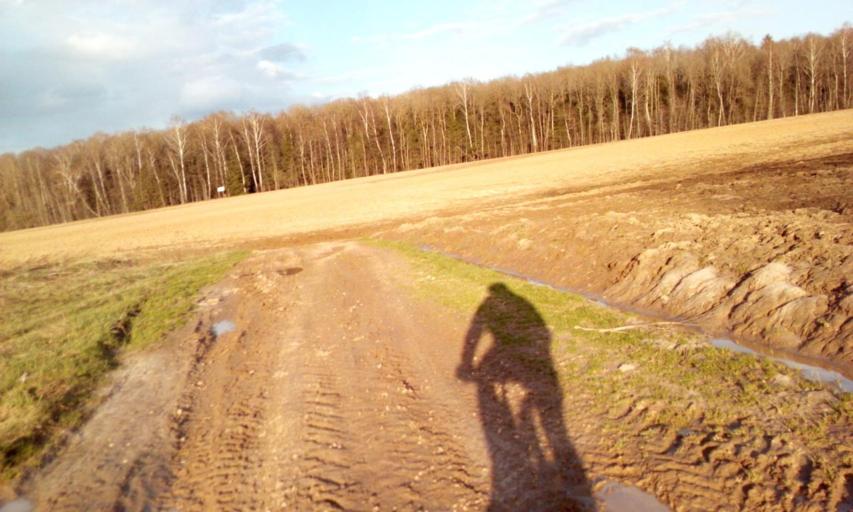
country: RU
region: Moskovskaya
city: Annino
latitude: 55.5497
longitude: 37.2351
